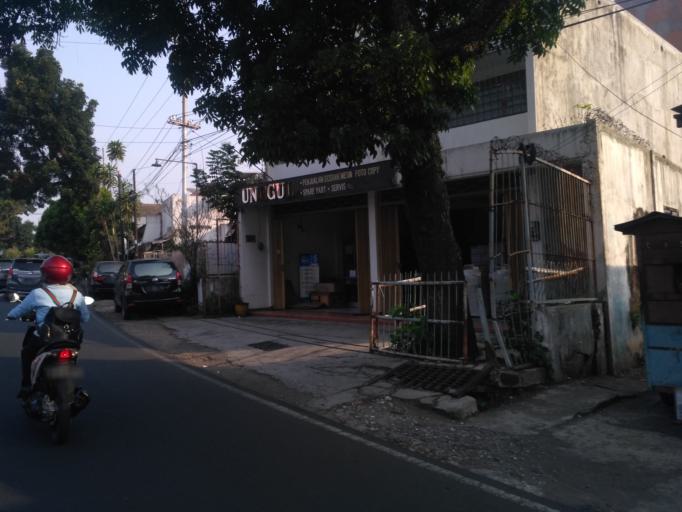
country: ID
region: East Java
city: Malang
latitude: -7.9668
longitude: 112.6288
